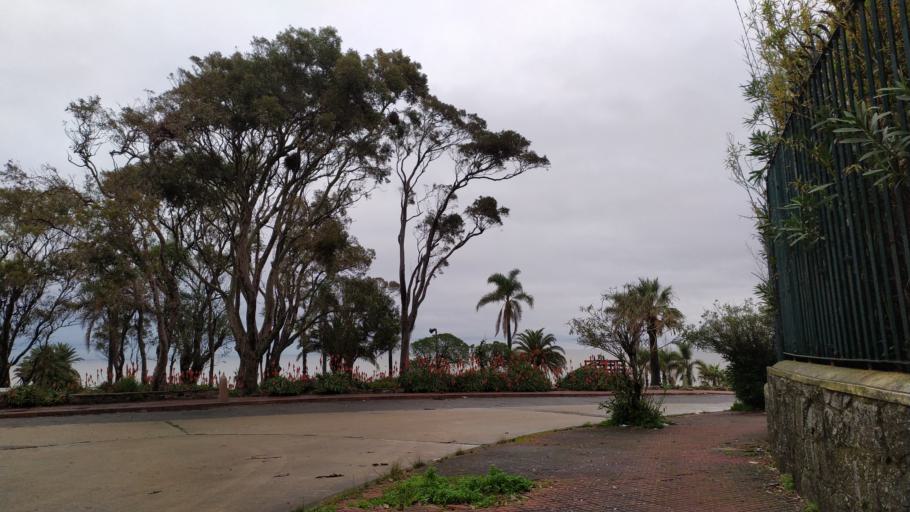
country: UY
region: Canelones
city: Paso de Carrasco
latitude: -34.8982
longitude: -56.0811
